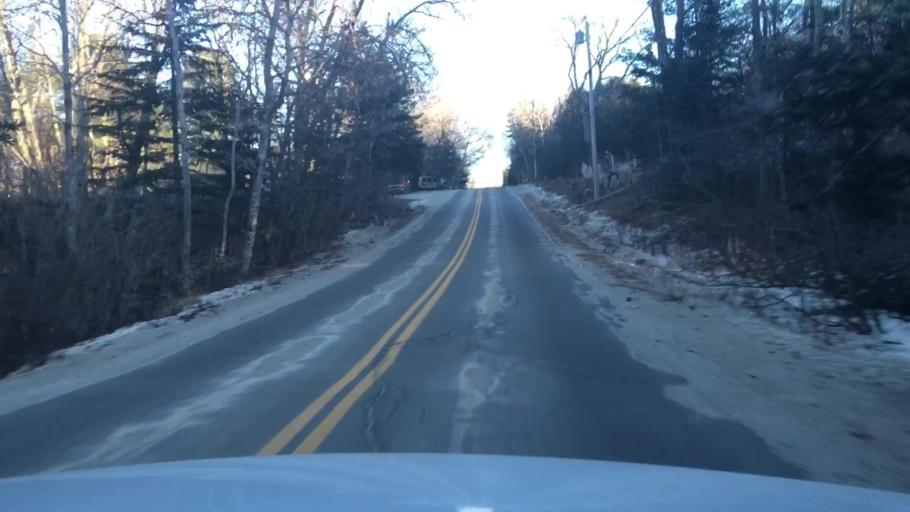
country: US
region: Maine
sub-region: Hancock County
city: Penobscot
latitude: 44.3899
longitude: -68.7038
